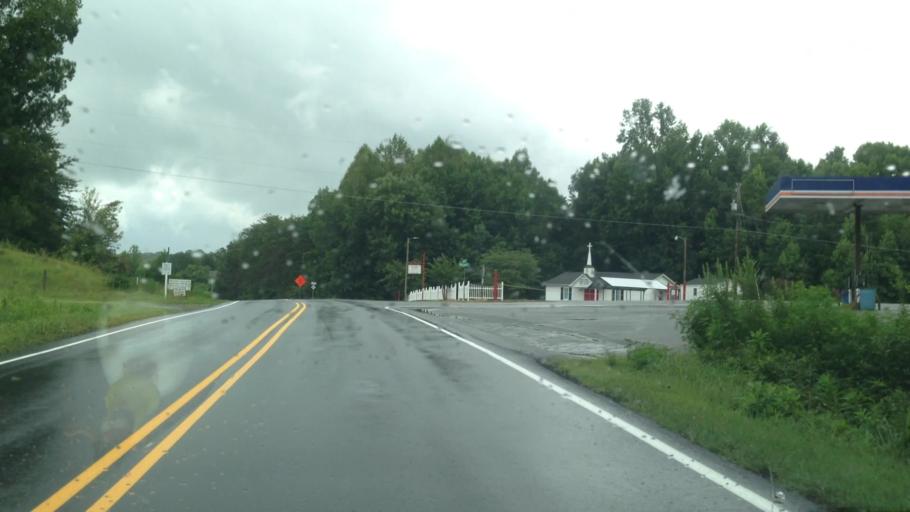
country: US
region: North Carolina
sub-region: Stokes County
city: Walnut Cove
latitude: 36.2497
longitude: -80.0968
